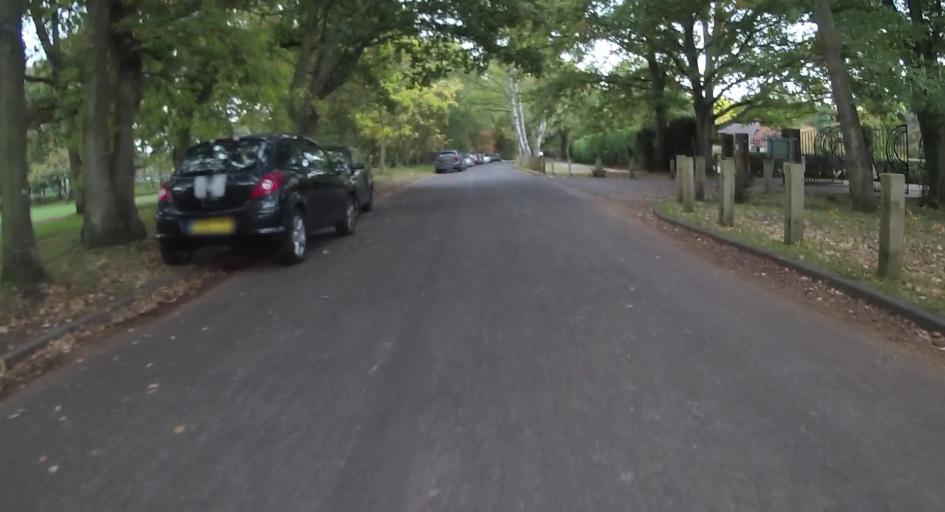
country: GB
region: England
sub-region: Bracknell Forest
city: Crowthorne
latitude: 51.3915
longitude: -0.7792
